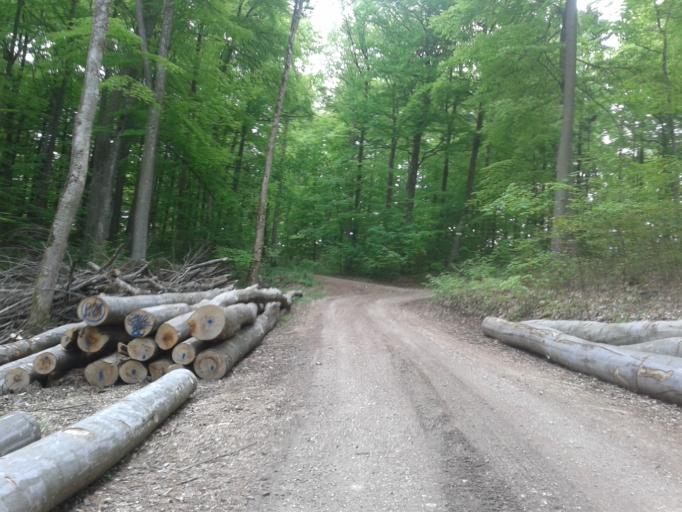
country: DE
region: Baden-Wuerttemberg
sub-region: Tuebingen Region
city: Blaubeuren
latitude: 48.3982
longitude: 9.7926
